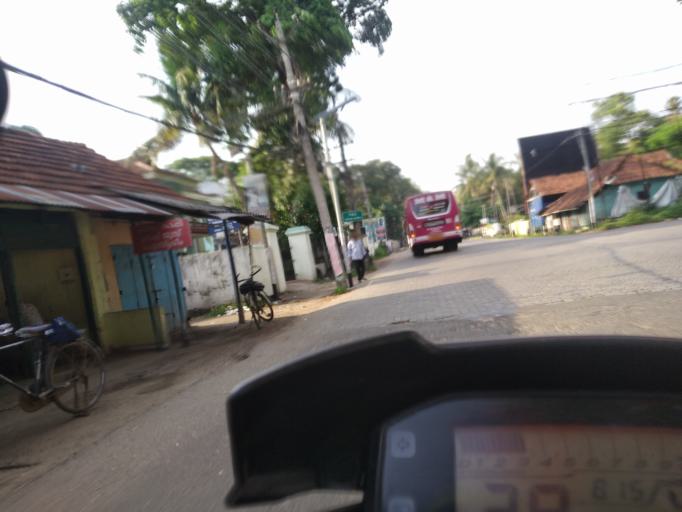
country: IN
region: Kerala
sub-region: Alappuzha
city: Arukutti
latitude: 9.9429
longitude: 76.3498
